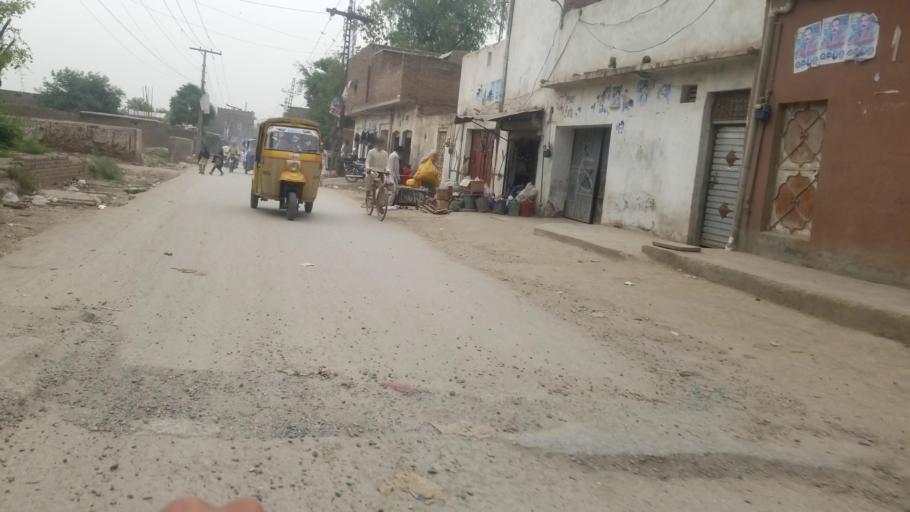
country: PK
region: Khyber Pakhtunkhwa
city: Peshawar
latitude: 33.9888
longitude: 71.5503
